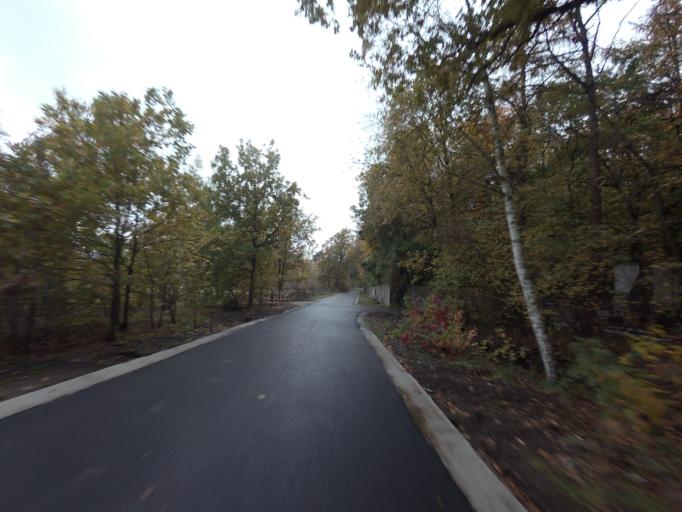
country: BE
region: Flanders
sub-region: Provincie Antwerpen
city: Bonheiden
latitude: 51.0140
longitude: 4.5581
